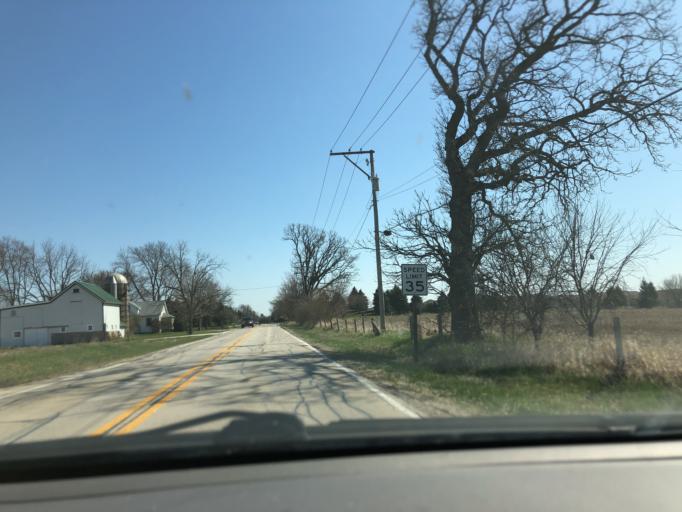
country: US
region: Illinois
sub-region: McHenry County
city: Huntley
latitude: 42.1628
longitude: -88.4565
